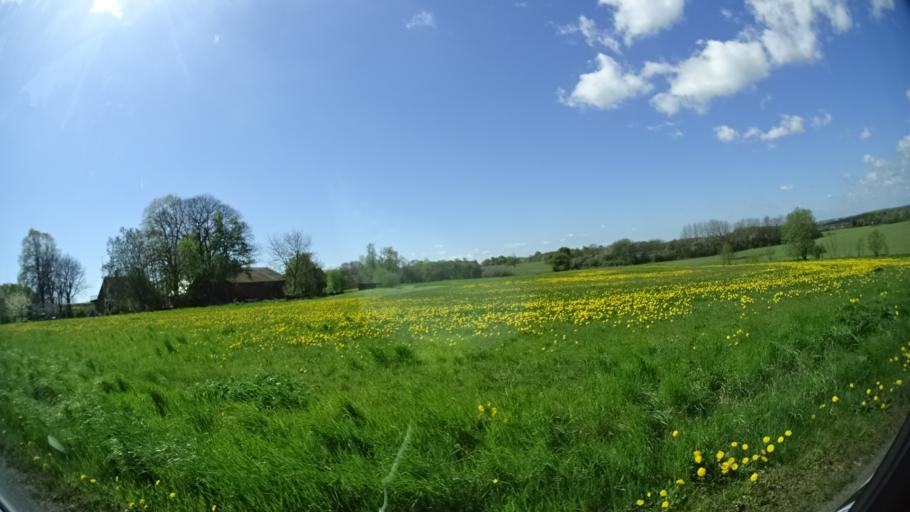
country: DK
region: Central Jutland
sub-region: Skanderborg Kommune
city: Horning
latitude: 56.1178
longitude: 10.0192
